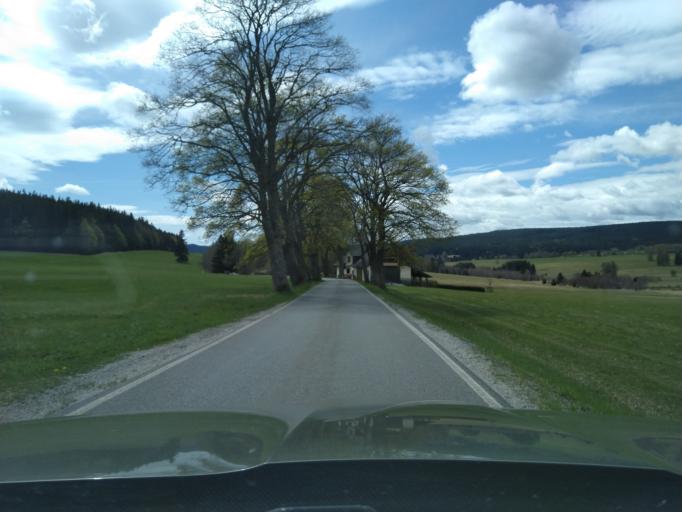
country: CZ
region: Jihocesky
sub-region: Okres Prachatice
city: Borova Lada
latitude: 49.0397
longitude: 13.6684
